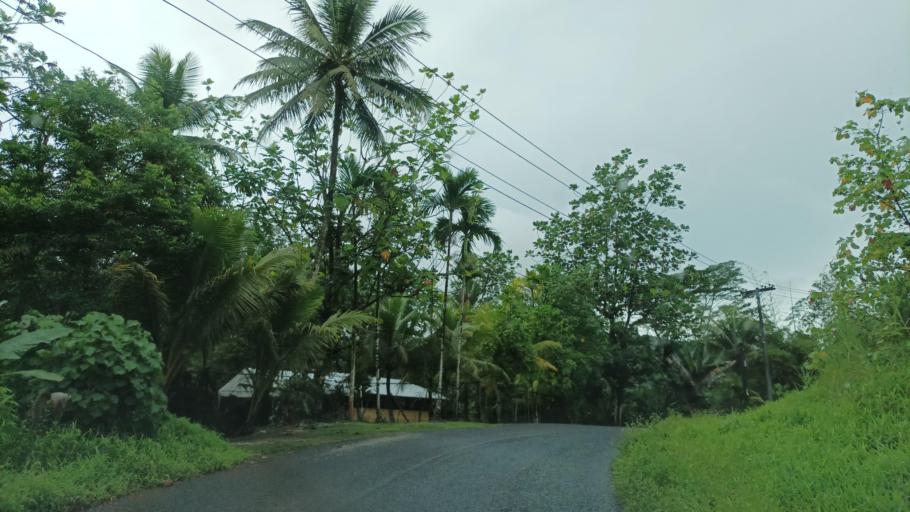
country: FM
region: Pohnpei
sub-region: Sokehs Municipality
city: Palikir - National Government Center
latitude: 6.8833
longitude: 158.1610
